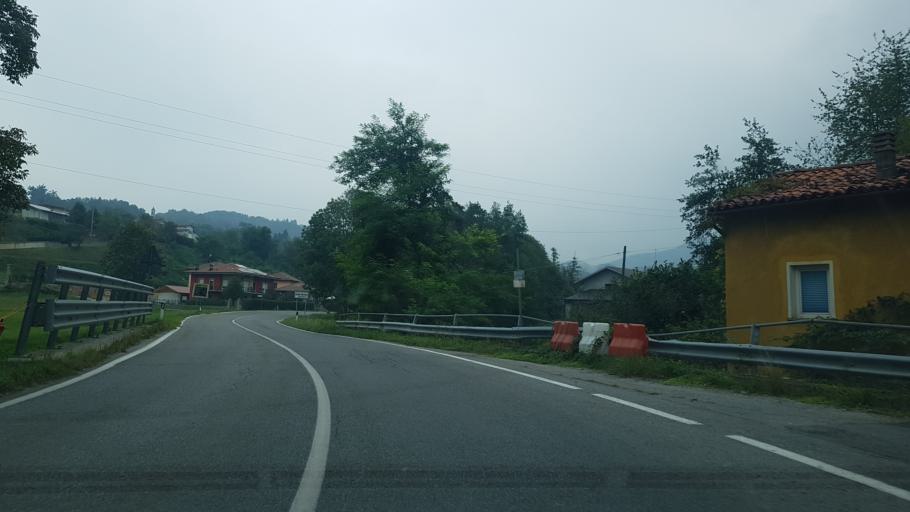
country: IT
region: Piedmont
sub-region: Provincia di Cuneo
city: Frabosa Sottana
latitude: 44.3287
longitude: 7.7889
